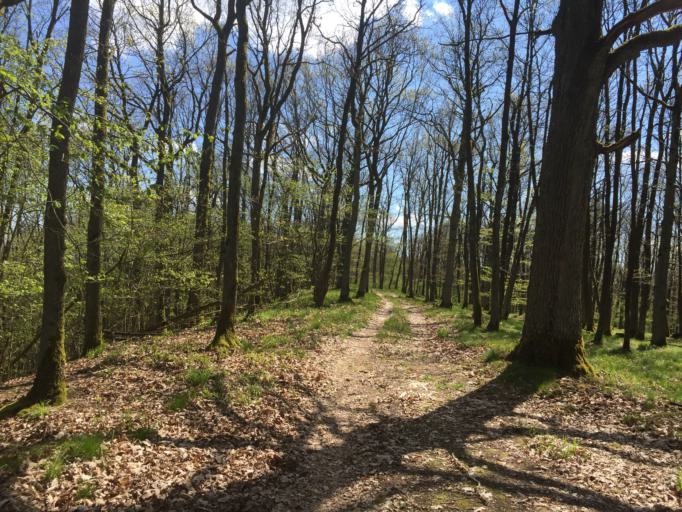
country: DE
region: Bavaria
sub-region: Regierungsbezirk Unterfranken
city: Sulzfeld
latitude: 50.2576
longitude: 10.4449
